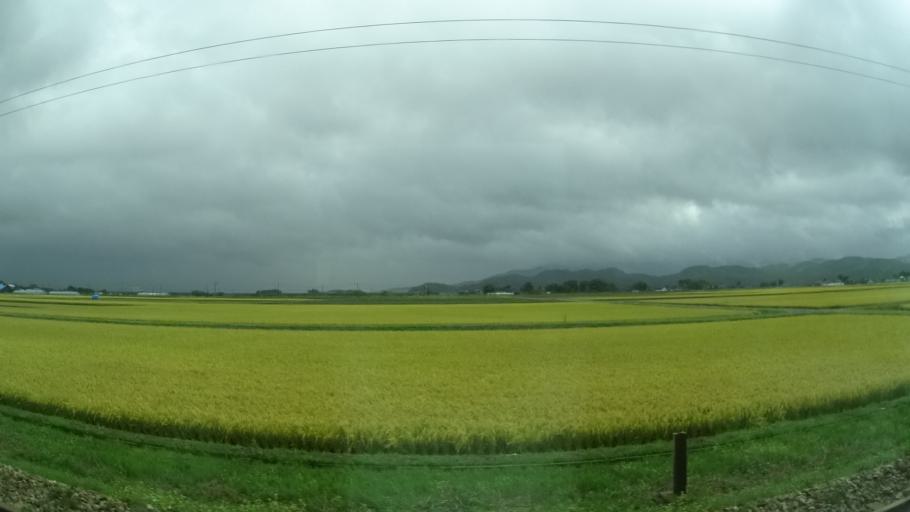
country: JP
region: Yamagata
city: Tsuruoka
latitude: 38.7264
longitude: 139.7453
